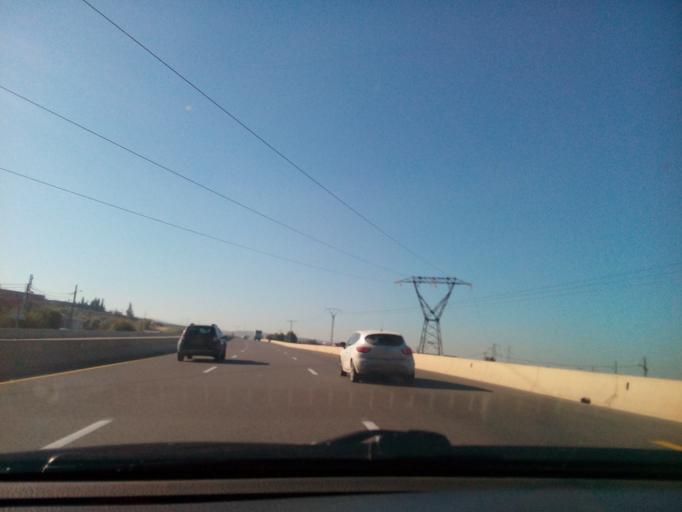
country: DZ
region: Chlef
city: Oued Sly
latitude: 36.0831
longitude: 1.1865
